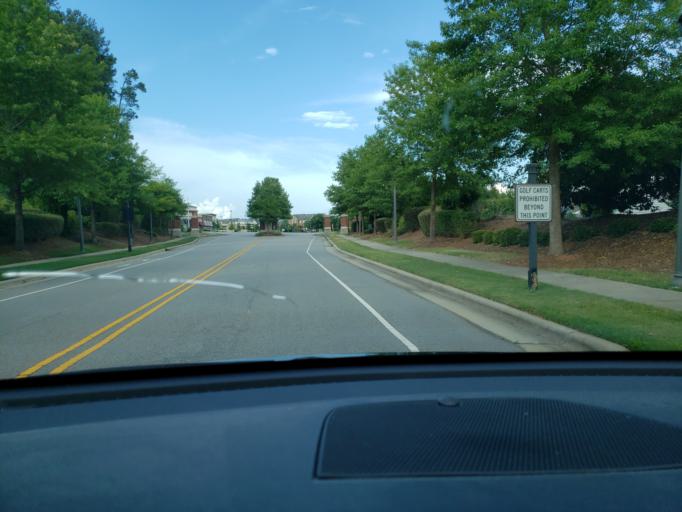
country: US
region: North Carolina
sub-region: Wake County
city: Green Level
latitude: 35.8289
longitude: -78.9112
